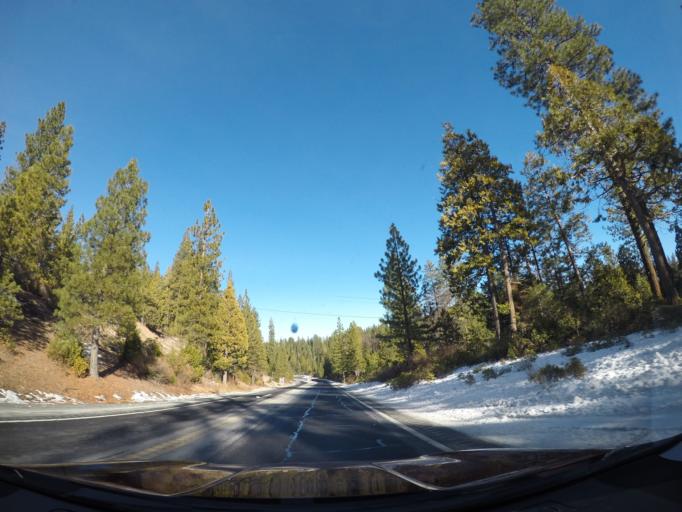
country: US
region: California
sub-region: Tuolumne County
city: Twain Harte
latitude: 38.0982
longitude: -120.1266
